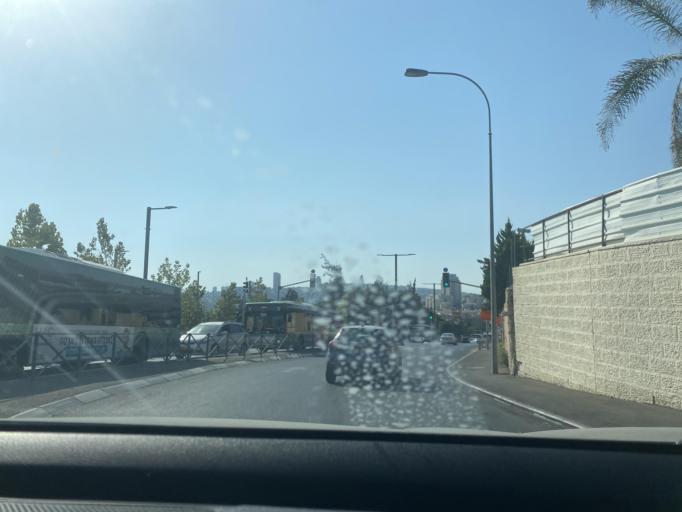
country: IL
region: Jerusalem
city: Jerusalem
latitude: 31.7467
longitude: 35.2132
